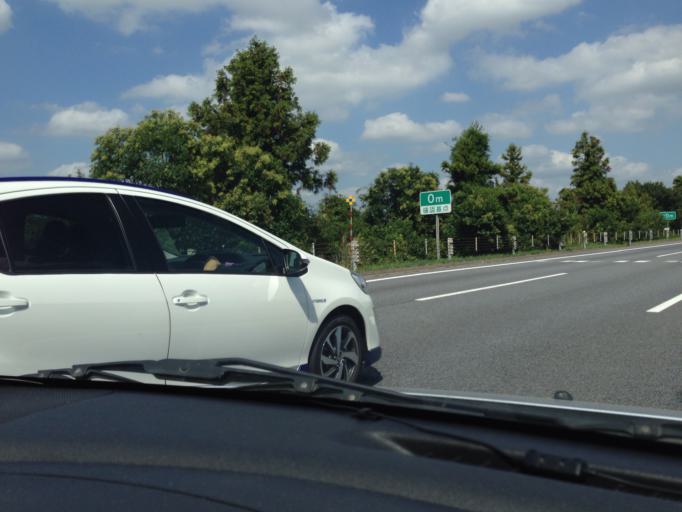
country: JP
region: Ibaraki
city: Naka
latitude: 36.0902
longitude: 140.1594
